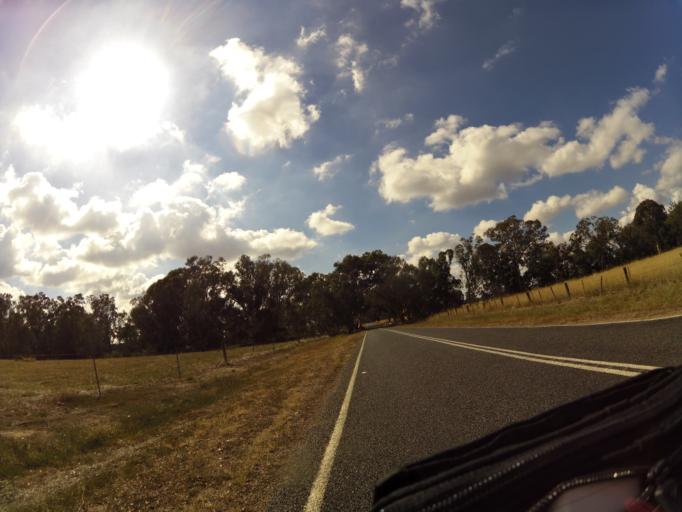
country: AU
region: Victoria
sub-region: Benalla
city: Benalla
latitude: -36.5797
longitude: 145.9953
